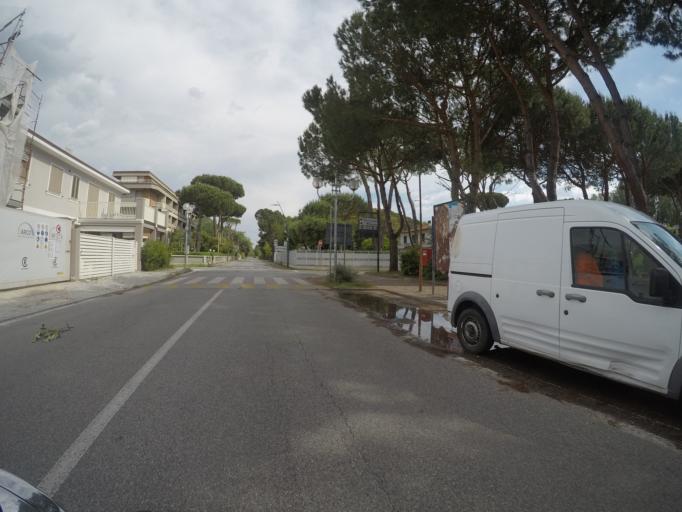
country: IT
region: Tuscany
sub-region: Provincia di Massa-Carrara
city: Capanne-Prato-Cinquale
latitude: 43.9777
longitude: 10.1471
